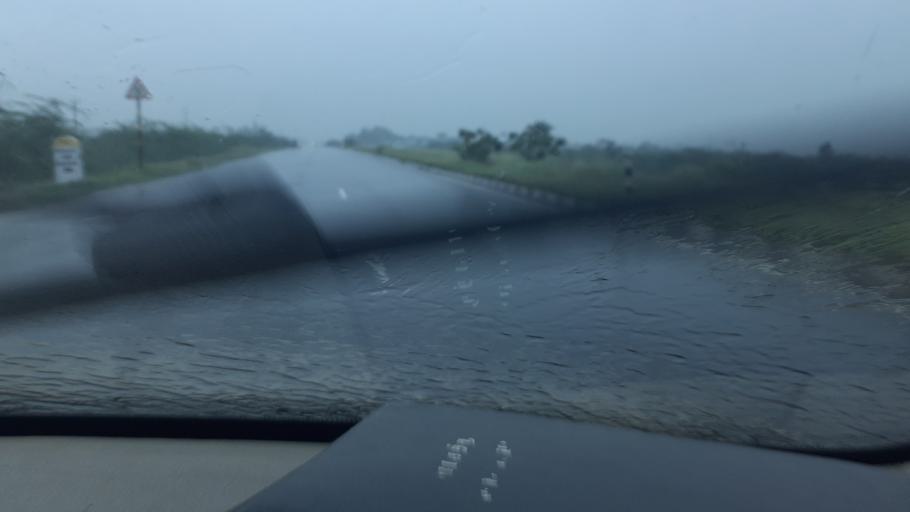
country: IN
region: Tamil Nadu
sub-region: Virudhunagar
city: Sattur
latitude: 9.4320
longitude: 77.9196
